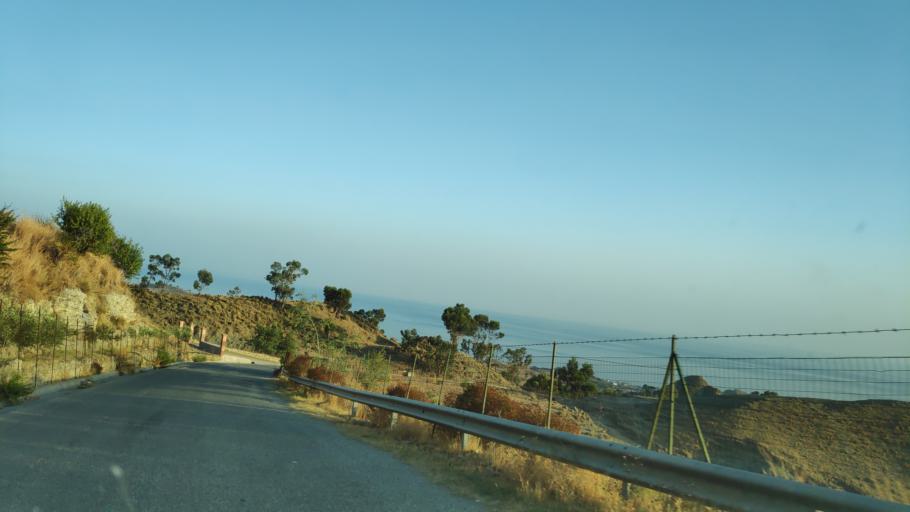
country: IT
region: Calabria
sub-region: Provincia di Reggio Calabria
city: Bova Marina
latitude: 37.9577
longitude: 15.9223
